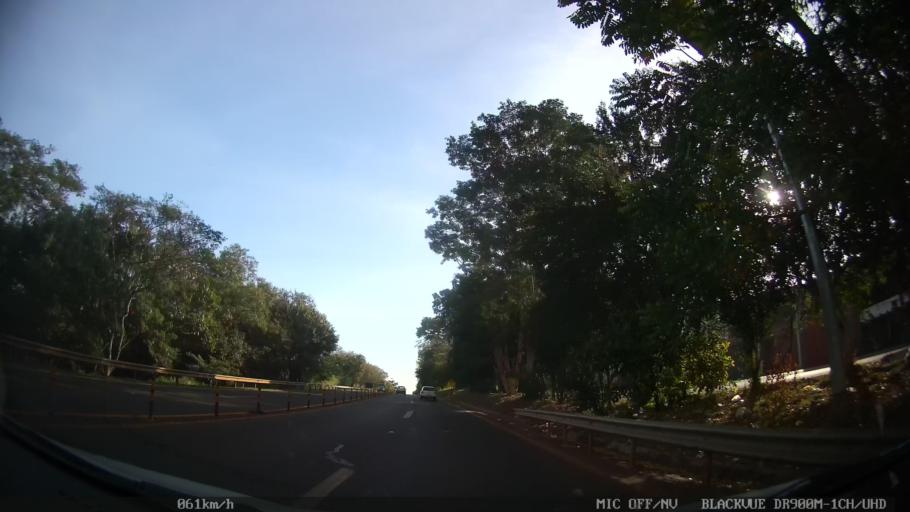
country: BR
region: Sao Paulo
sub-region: Ribeirao Preto
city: Ribeirao Preto
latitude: -21.2614
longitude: -47.8185
